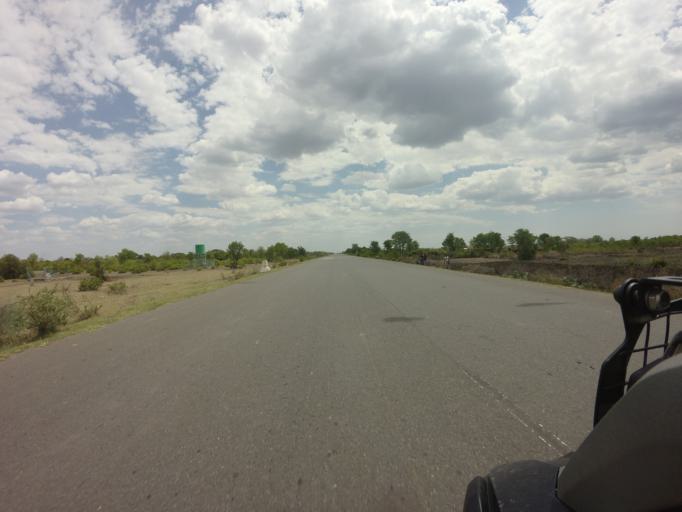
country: AO
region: Huila
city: Lubango
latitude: -15.4889
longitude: 14.0528
